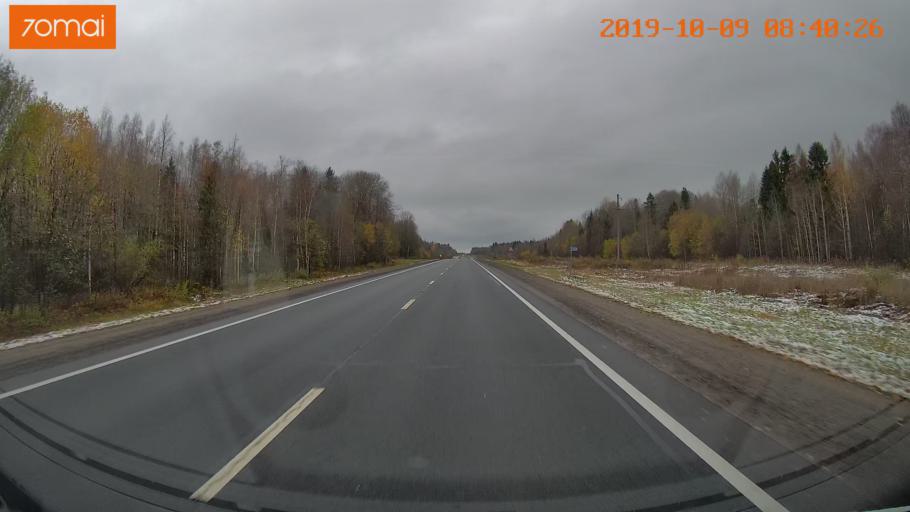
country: RU
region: Vologda
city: Gryazovets
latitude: 58.9865
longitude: 40.1404
